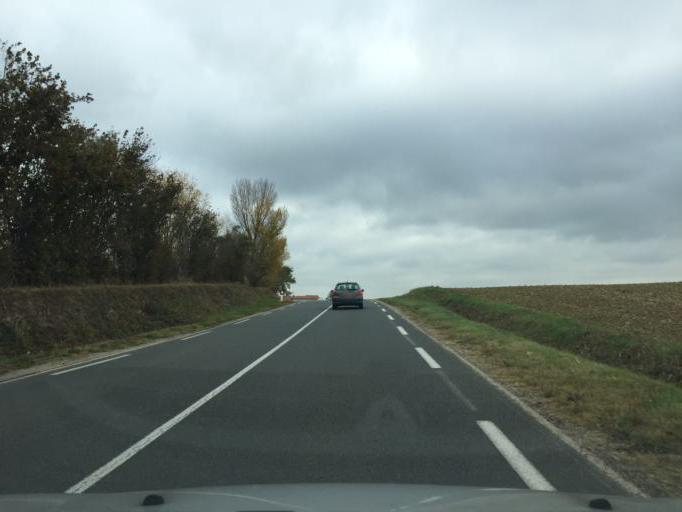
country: FR
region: Rhone-Alpes
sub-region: Departement de l'Ain
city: Reyrieux
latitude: 45.9387
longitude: 4.8531
